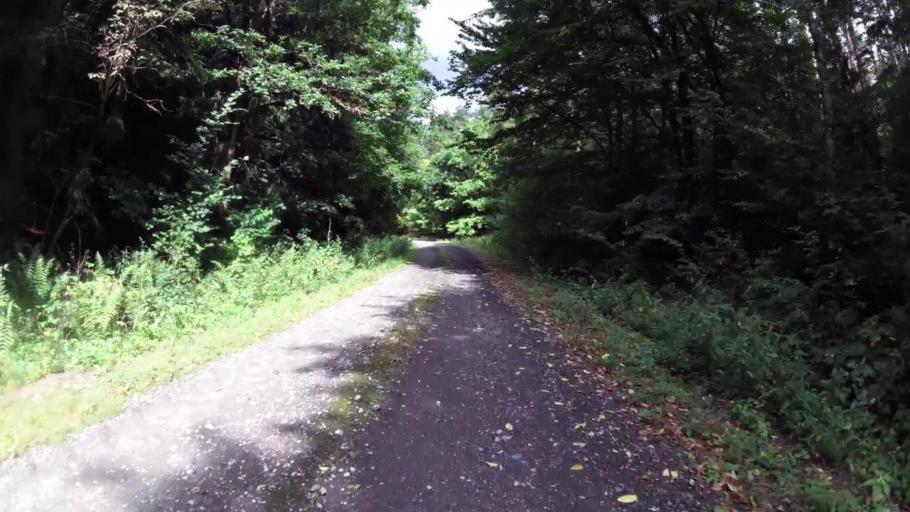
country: PL
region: West Pomeranian Voivodeship
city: Trzcinsko Zdroj
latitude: 52.8821
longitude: 14.6819
